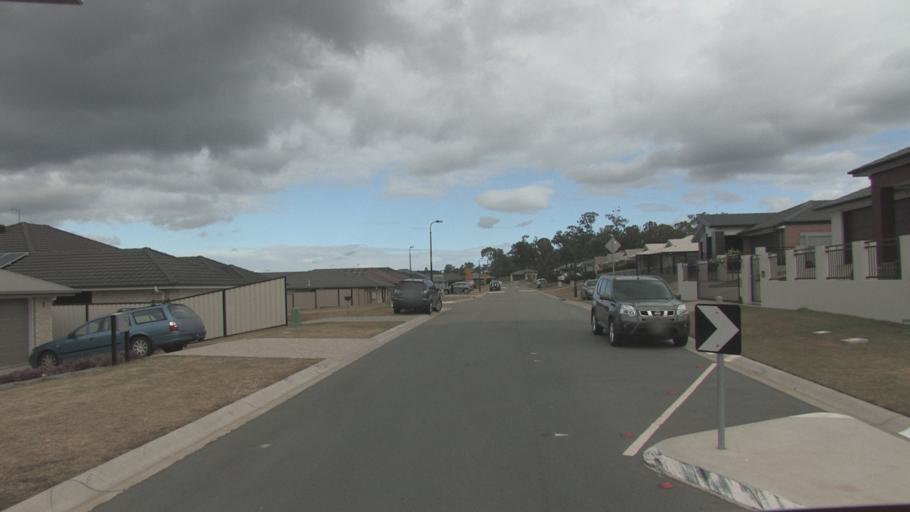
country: AU
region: Queensland
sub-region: Logan
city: Park Ridge South
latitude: -27.6867
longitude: 153.0479
